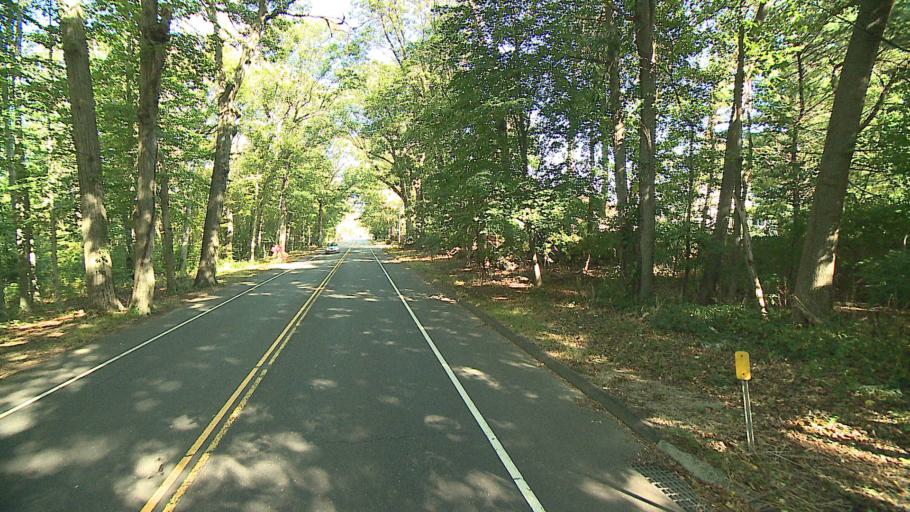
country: US
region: Connecticut
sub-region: Fairfield County
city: New Canaan
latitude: 41.1257
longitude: -73.4850
